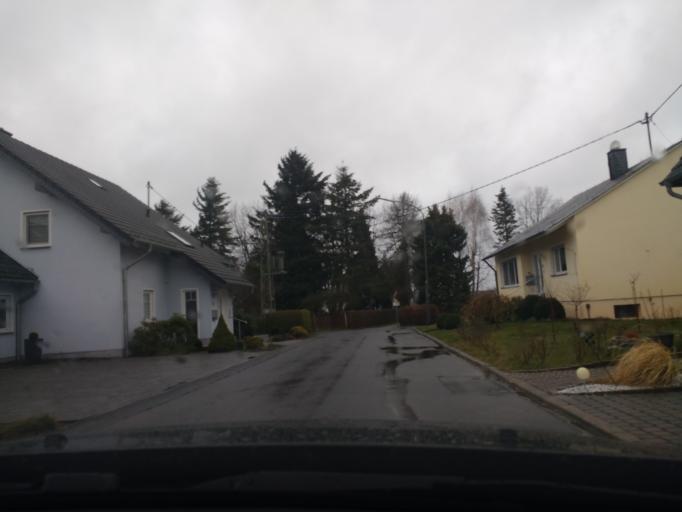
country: DE
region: Rheinland-Pfalz
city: Irmenach
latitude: 49.9229
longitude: 7.1908
